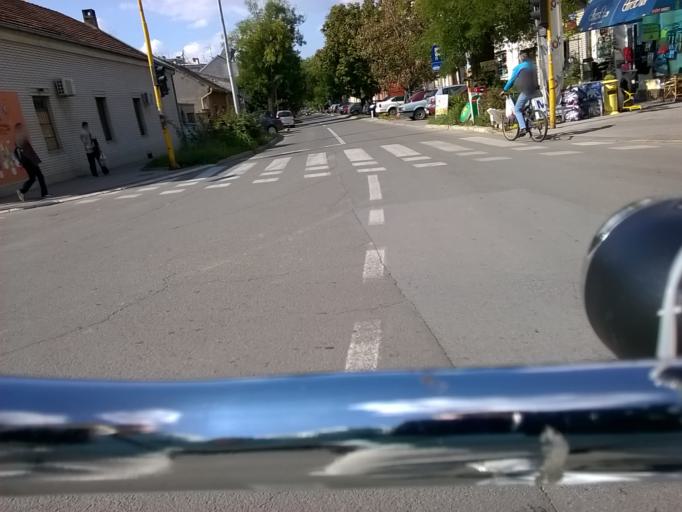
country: RS
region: Autonomna Pokrajina Vojvodina
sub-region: Juznobanatski Okrug
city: Pancevo
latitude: 44.8731
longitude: 20.6434
